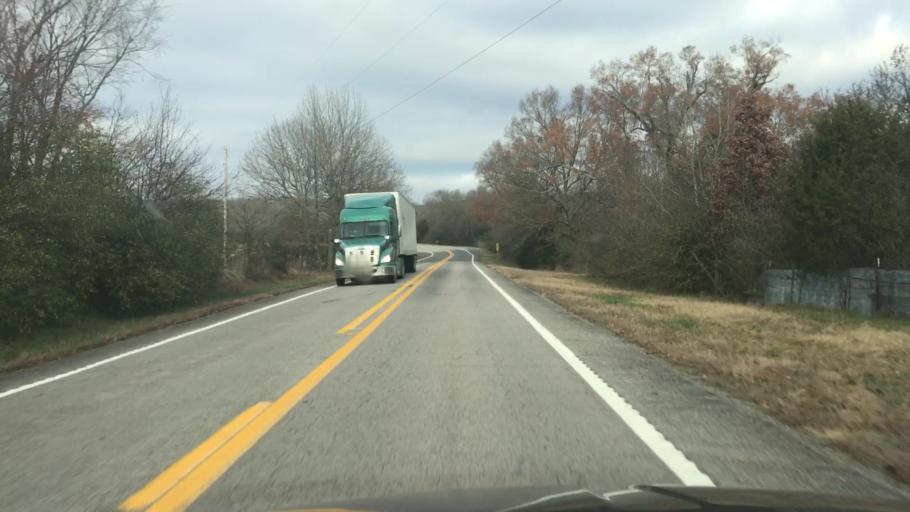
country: US
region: Arkansas
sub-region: Montgomery County
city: Mount Ida
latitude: 34.6574
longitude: -93.7608
